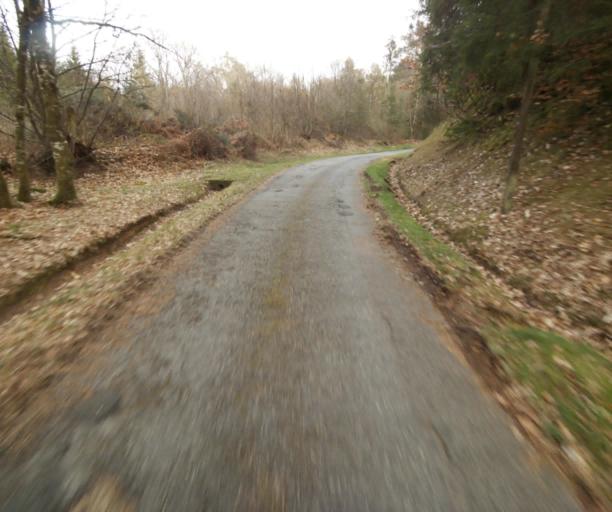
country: FR
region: Limousin
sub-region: Departement de la Correze
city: Argentat
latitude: 45.2233
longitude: 1.9635
